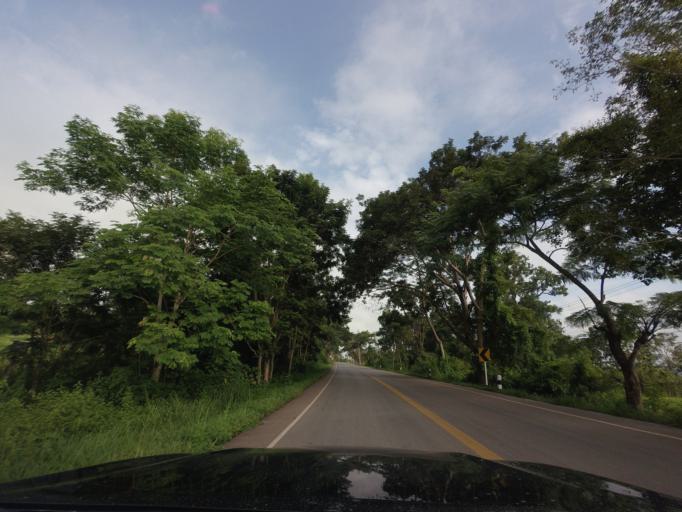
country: TH
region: Changwat Udon Thani
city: Nam Som
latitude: 17.8358
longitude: 102.2602
